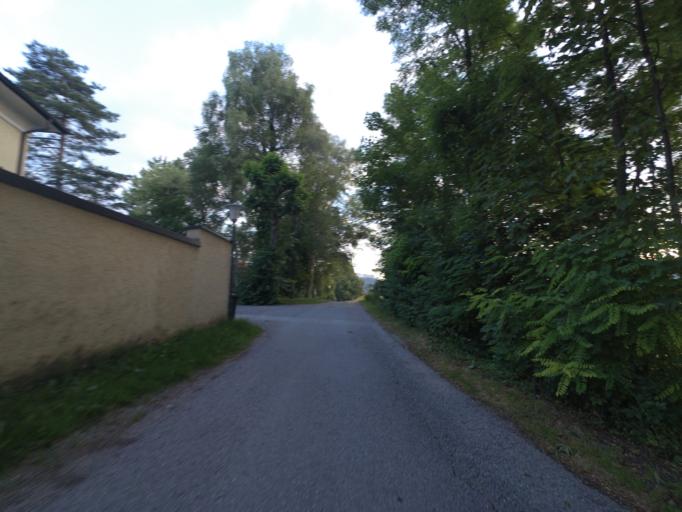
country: AT
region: Salzburg
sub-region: Salzburg Stadt
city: Salzburg
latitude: 47.7753
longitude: 13.0527
